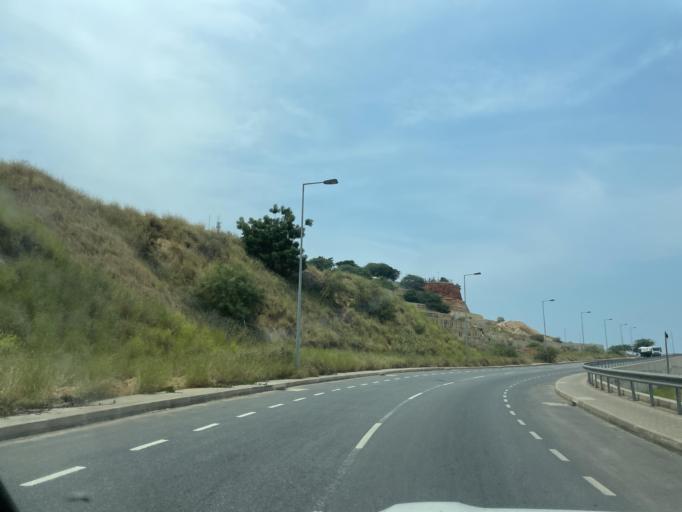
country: AO
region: Luanda
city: Luanda
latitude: -8.8071
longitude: 13.2524
